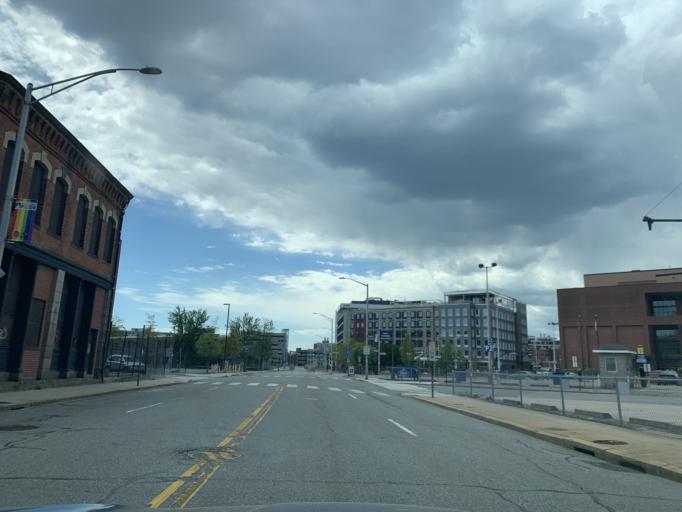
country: US
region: Rhode Island
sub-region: Providence County
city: Providence
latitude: 41.8228
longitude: -71.4083
